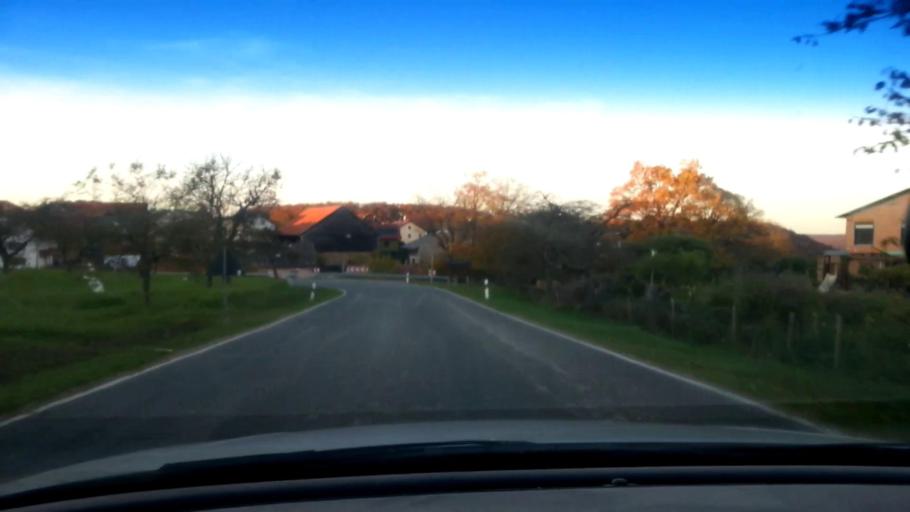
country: DE
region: Bavaria
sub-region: Upper Franconia
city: Heiligenstadt
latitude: 49.8553
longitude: 11.1172
